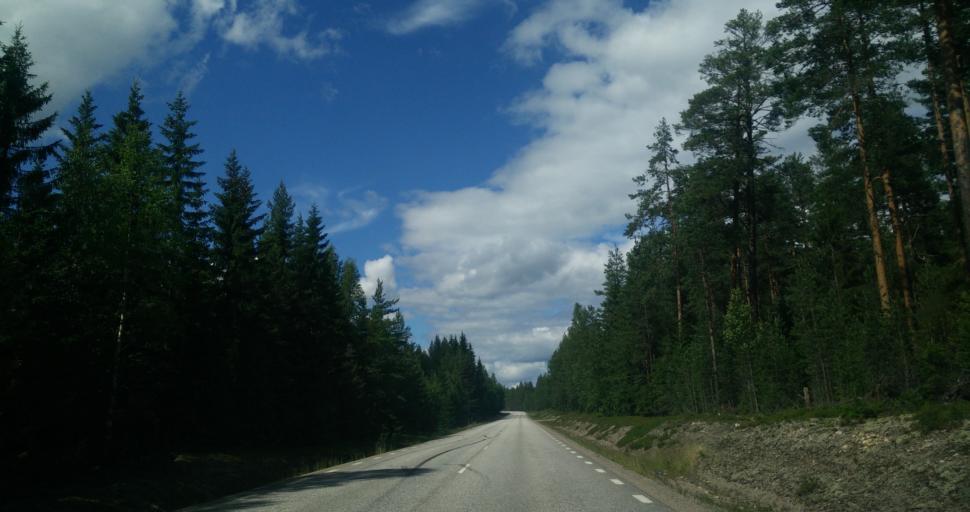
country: SE
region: Gaevleborg
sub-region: Nordanstigs Kommun
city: Bergsjoe
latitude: 62.0276
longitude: 16.9141
